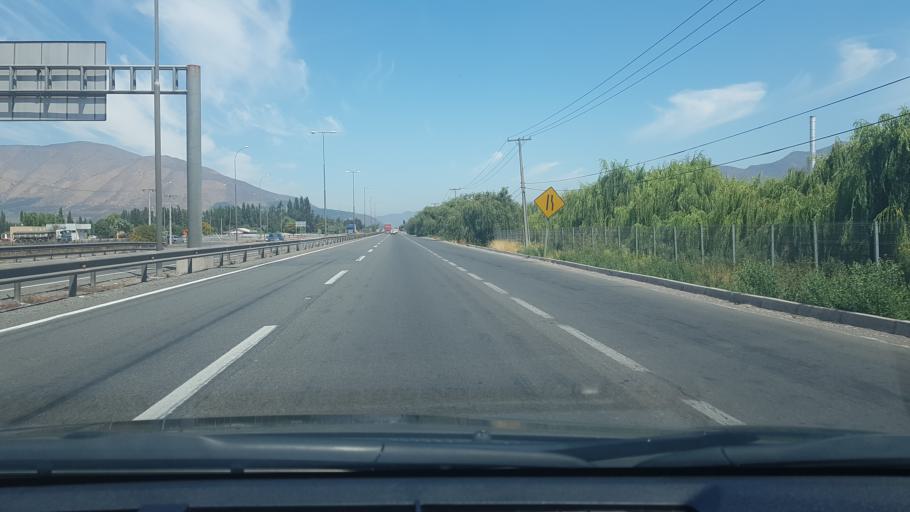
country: CL
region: Valparaiso
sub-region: Provincia de San Felipe
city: Llaillay
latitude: -32.8507
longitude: -70.9444
